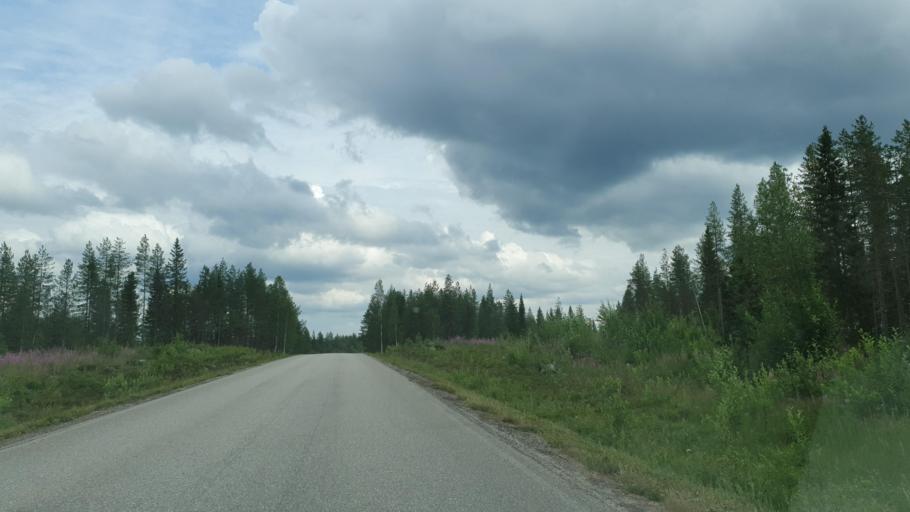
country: FI
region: Kainuu
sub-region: Kehys-Kainuu
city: Kuhmo
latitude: 64.5973
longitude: 29.8031
